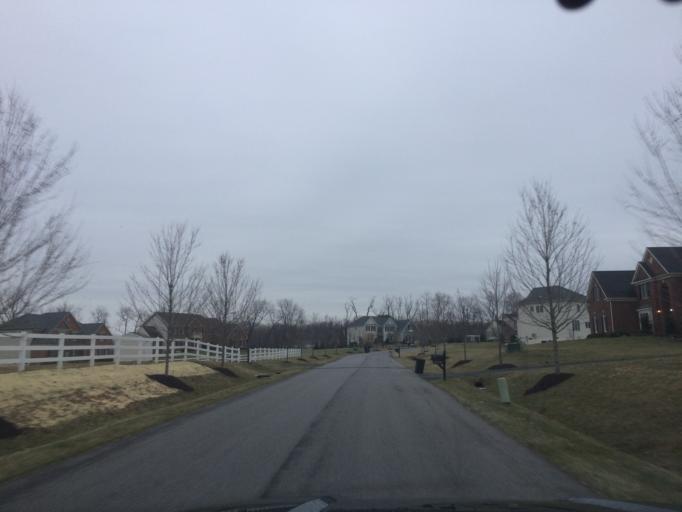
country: US
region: Maryland
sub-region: Howard County
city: Highland
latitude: 39.2672
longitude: -77.0029
